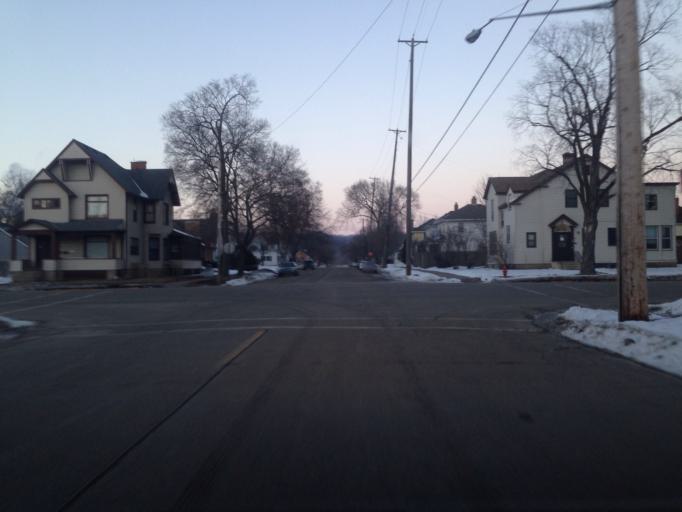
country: US
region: Minnesota
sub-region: Winona County
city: Winona
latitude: 44.0522
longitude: -91.6488
